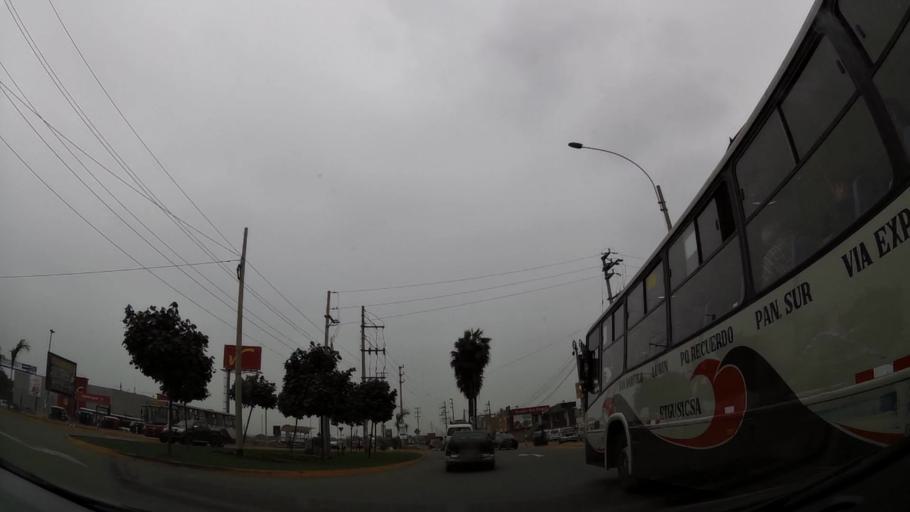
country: PE
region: Lima
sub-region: Lima
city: Punta Hermosa
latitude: -12.2741
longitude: -76.8722
